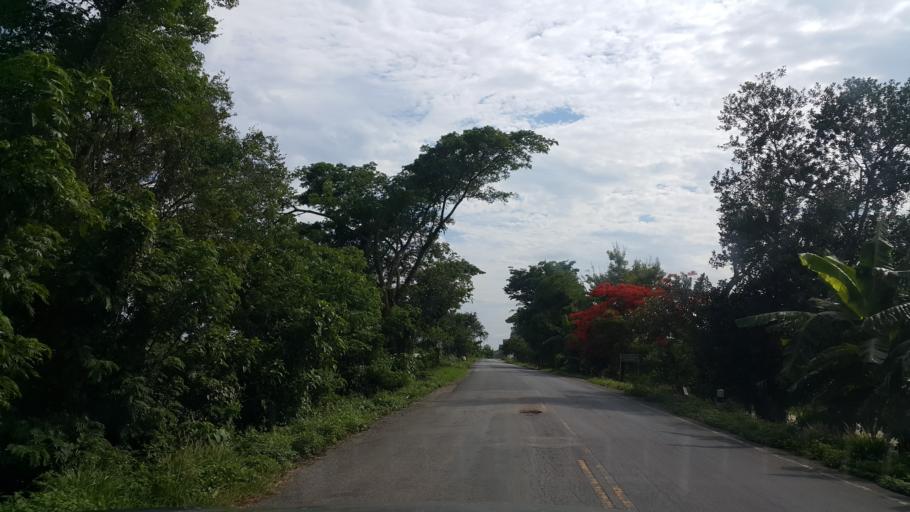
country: TH
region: Chiang Rai
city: Wiang Chai
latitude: 19.9570
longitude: 99.9369
